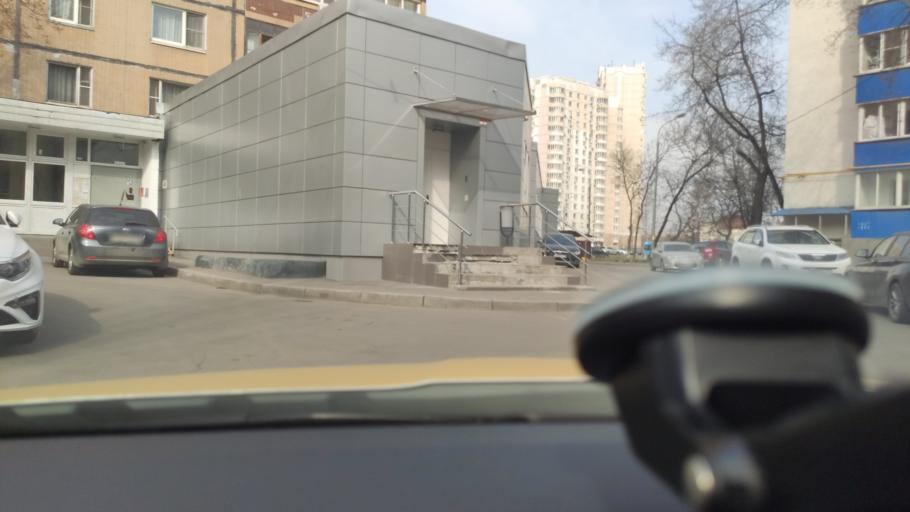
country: RU
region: Moscow
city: Novyye Kuz'minki
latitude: 55.7114
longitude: 37.7558
